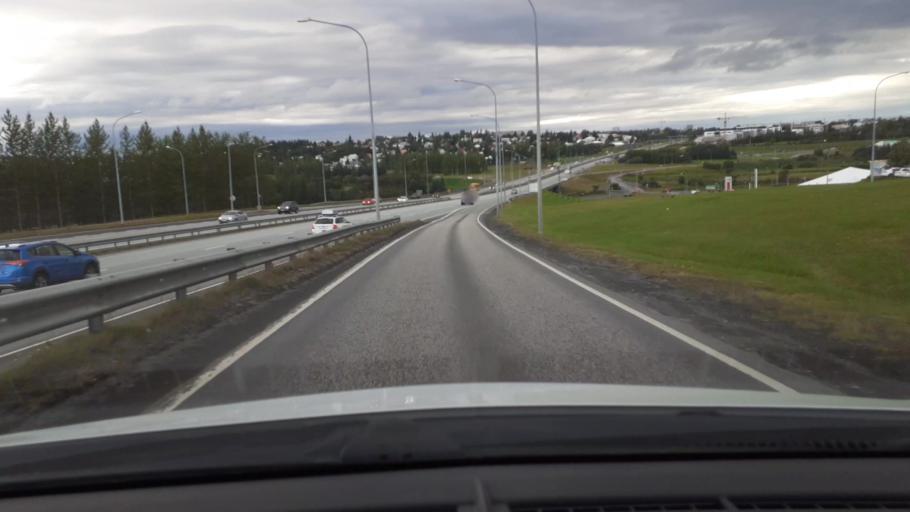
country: IS
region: Capital Region
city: Reykjavik
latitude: 64.1241
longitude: -21.8338
